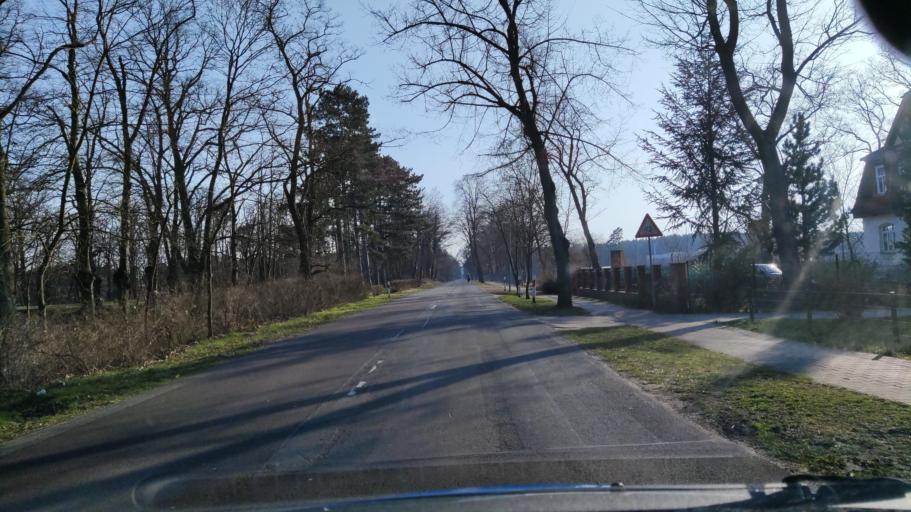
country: DE
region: Saxony-Anhalt
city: Seehausen
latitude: 52.8784
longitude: 11.7454
